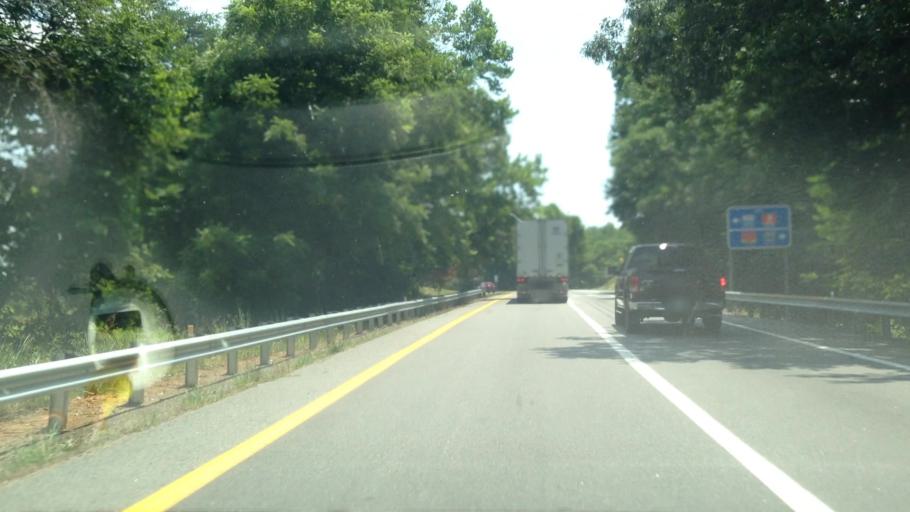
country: US
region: Virginia
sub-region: Henry County
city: Chatmoss
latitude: 36.6225
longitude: -79.8619
